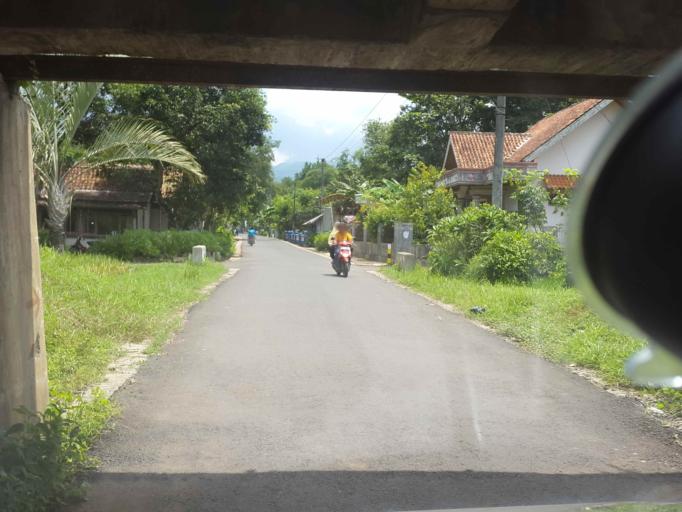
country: ID
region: Central Java
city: Rawaseser
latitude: -7.6143
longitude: 109.3754
